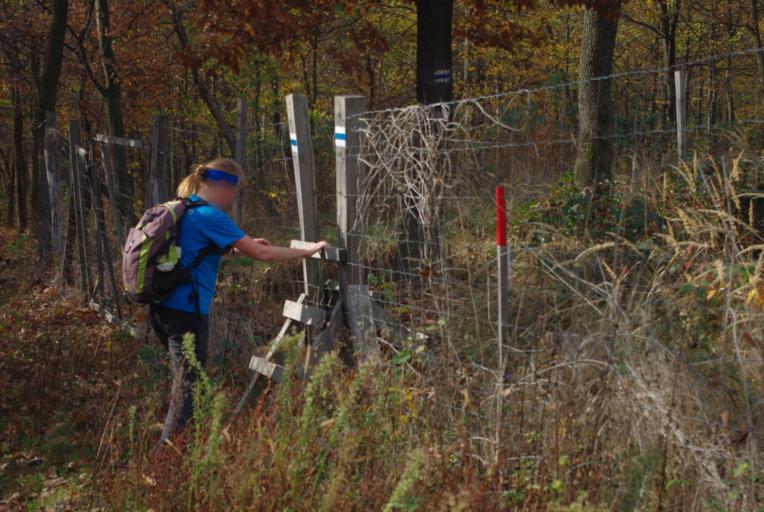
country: HU
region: Borsod-Abauj-Zemplen
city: Sarospatak
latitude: 48.3881
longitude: 21.5575
